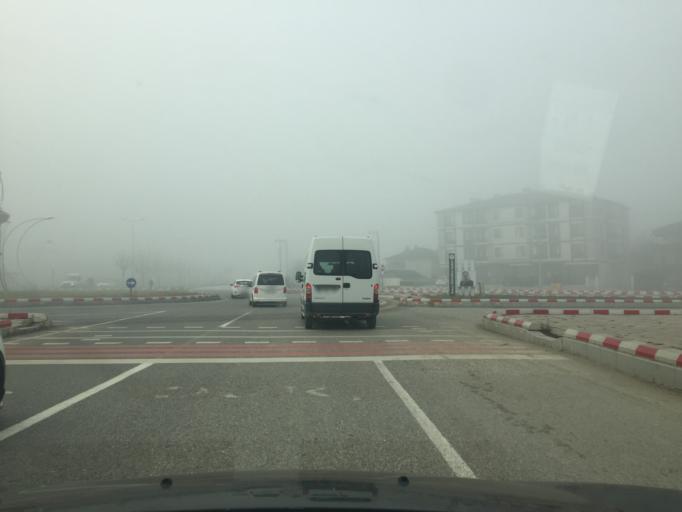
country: TR
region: Duzce
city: Duzce
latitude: 40.8416
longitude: 31.1806
